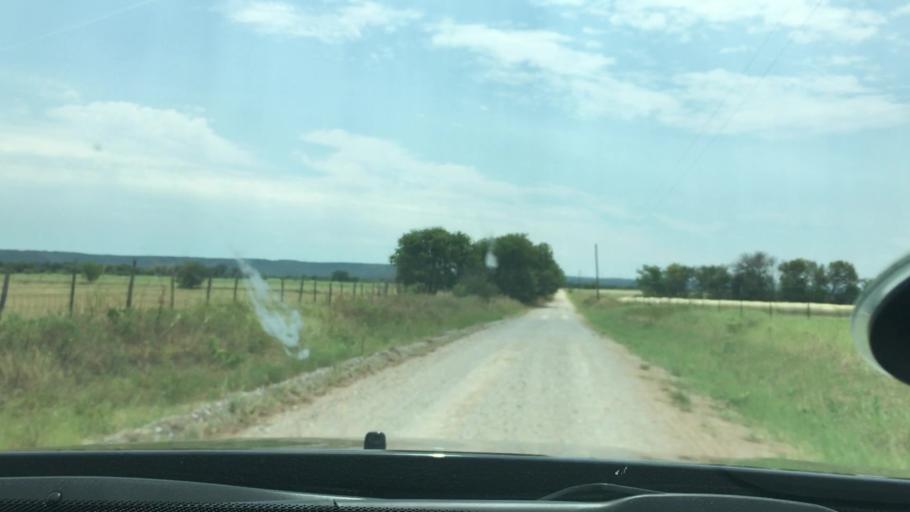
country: US
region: Texas
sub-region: Cooke County
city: Muenster
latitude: 33.8688
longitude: -97.3871
